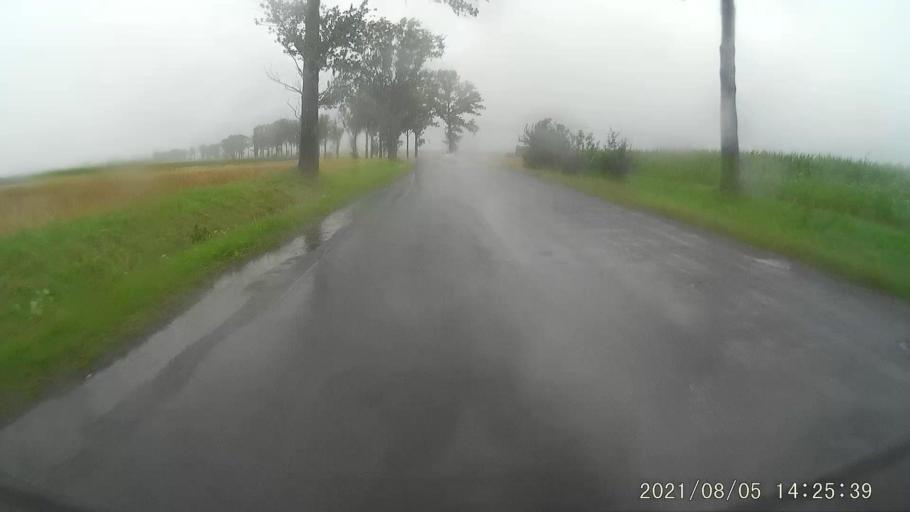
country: PL
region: Opole Voivodeship
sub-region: Powiat nyski
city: Korfantow
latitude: 50.4838
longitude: 17.6120
